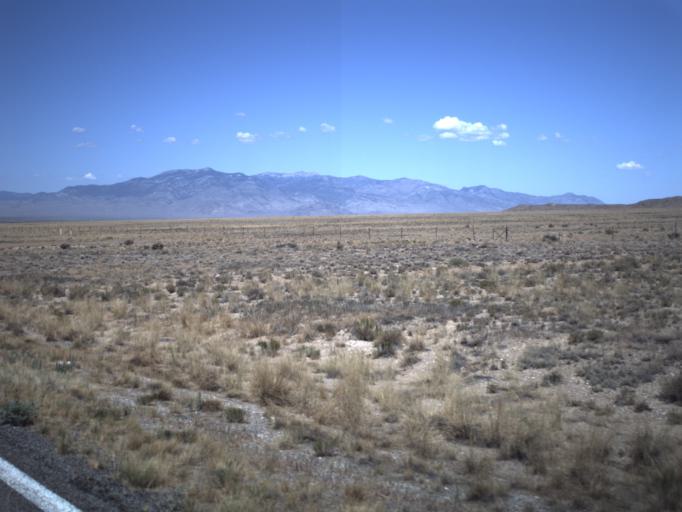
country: US
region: Nevada
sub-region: White Pine County
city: McGill
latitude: 39.0419
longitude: -113.8510
